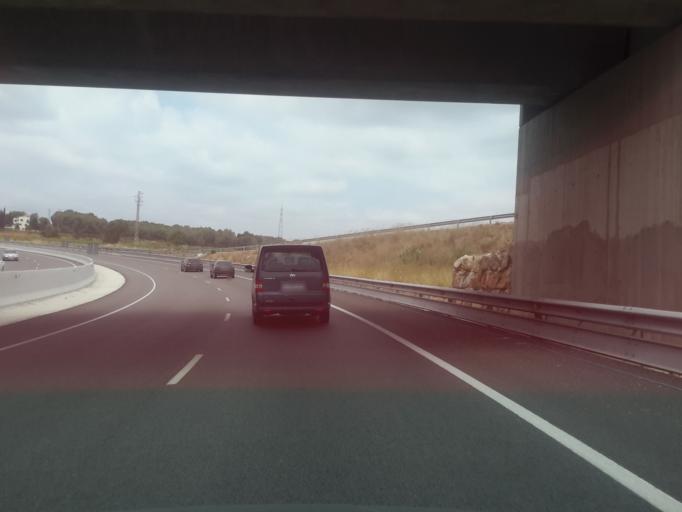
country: ES
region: Catalonia
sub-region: Provincia de Barcelona
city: Vilafranca del Penedes
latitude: 41.3214
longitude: 1.7258
